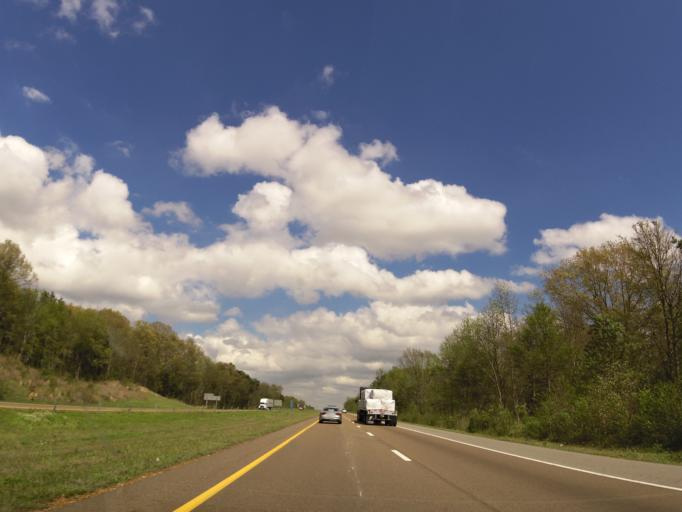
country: US
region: Tennessee
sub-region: Shelby County
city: Arlington
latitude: 35.2734
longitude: -89.6433
